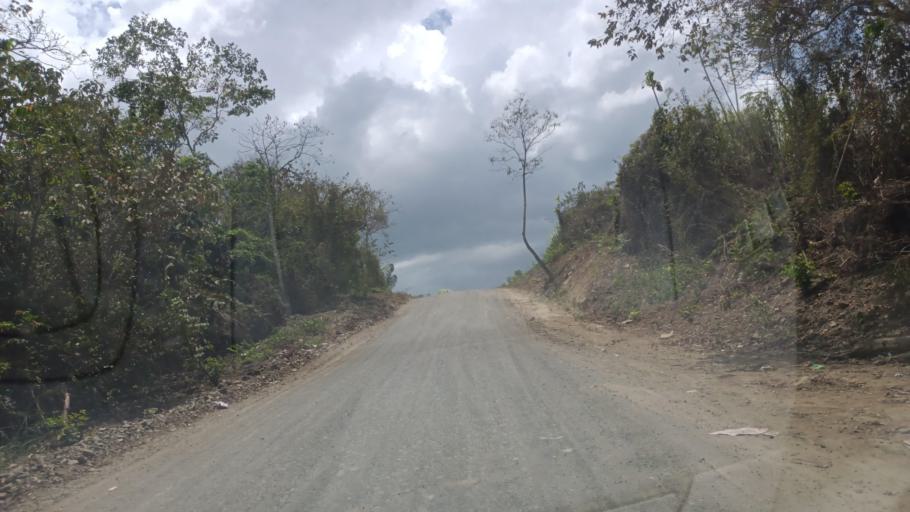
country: PA
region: Panama
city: Alcalde Diaz
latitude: 9.0924
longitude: -79.5775
